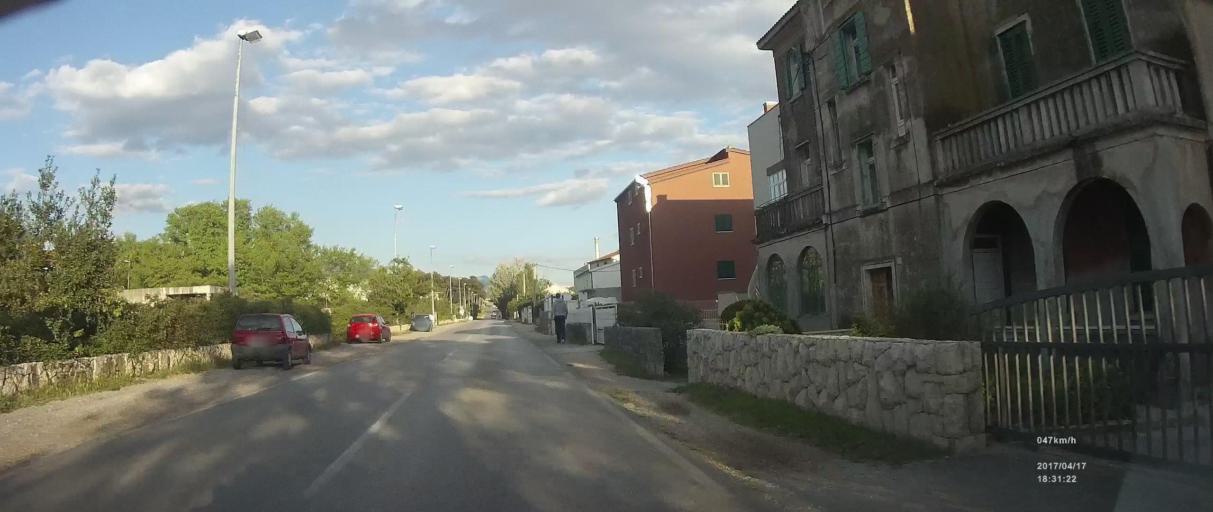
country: HR
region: Splitsko-Dalmatinska
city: Vranjic
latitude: 43.5452
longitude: 16.4336
